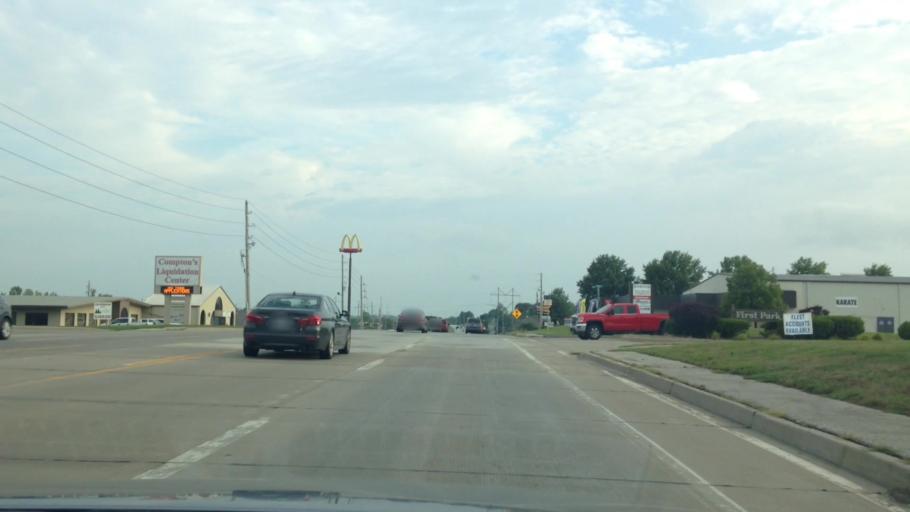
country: US
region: Missouri
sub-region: Clay County
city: Smithville
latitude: 39.3646
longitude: -94.5837
